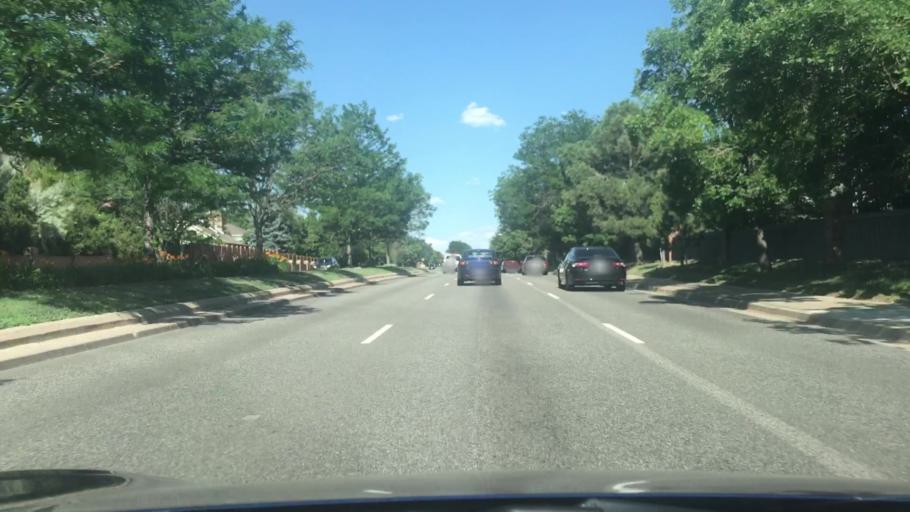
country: US
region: Colorado
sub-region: Arapahoe County
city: Dove Valley
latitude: 39.6530
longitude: -104.8260
